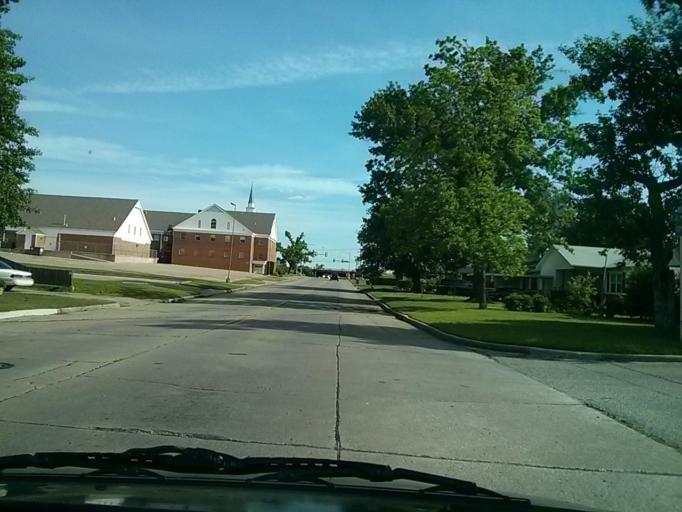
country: US
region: Oklahoma
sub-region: Tulsa County
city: Tulsa
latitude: 36.1588
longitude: -95.8956
